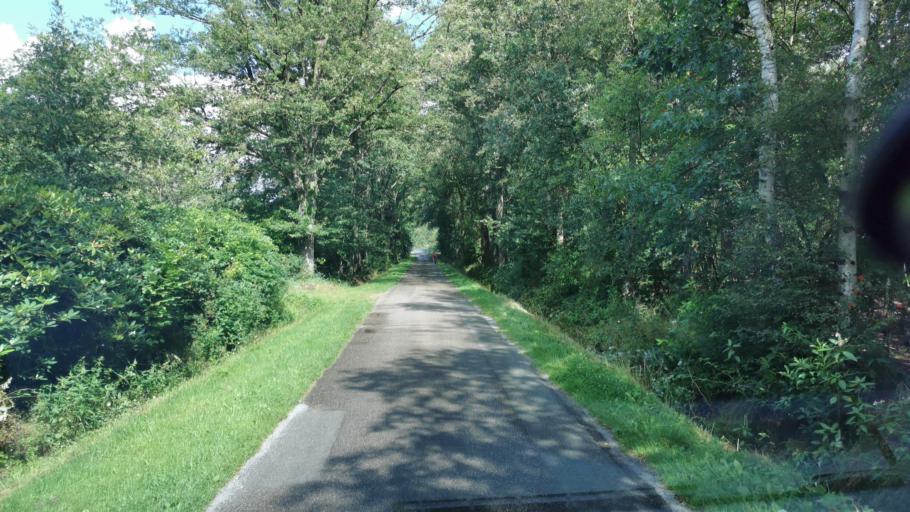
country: NL
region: Overijssel
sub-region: Gemeente Haaksbergen
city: Haaksbergen
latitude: 52.1375
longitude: 6.7409
